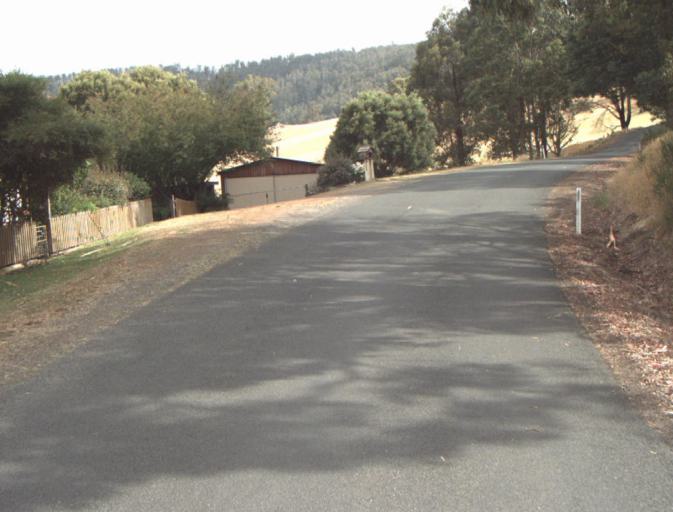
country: AU
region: Tasmania
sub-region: Dorset
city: Scottsdale
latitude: -41.4588
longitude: 147.5957
